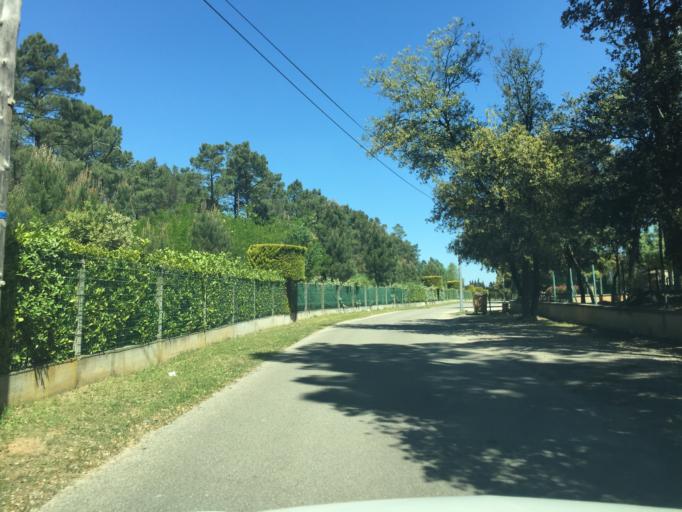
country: FR
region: Provence-Alpes-Cote d'Azur
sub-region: Departement du Vaucluse
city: Orange
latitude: 44.1048
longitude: 4.7982
